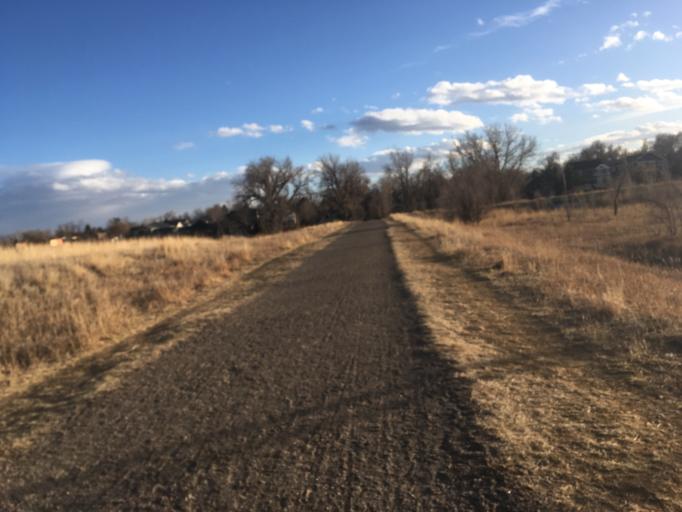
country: US
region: Colorado
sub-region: Boulder County
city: Lafayette
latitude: 40.0042
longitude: -105.0840
